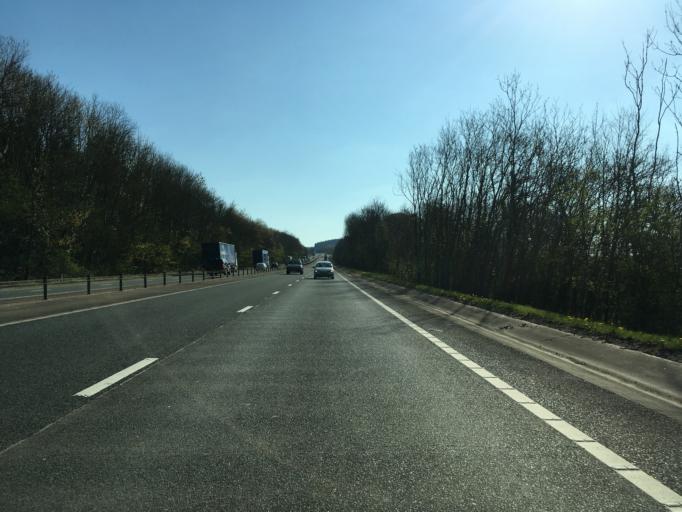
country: GB
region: Wales
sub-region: Newport
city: Langstone
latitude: 51.6311
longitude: -2.8935
